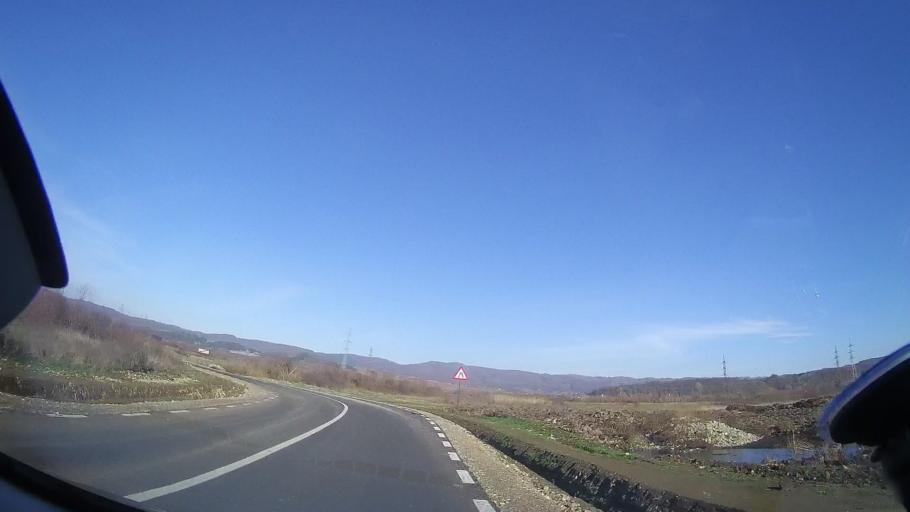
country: RO
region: Bihor
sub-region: Comuna Auseu
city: Auseu
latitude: 47.0080
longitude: 22.5025
